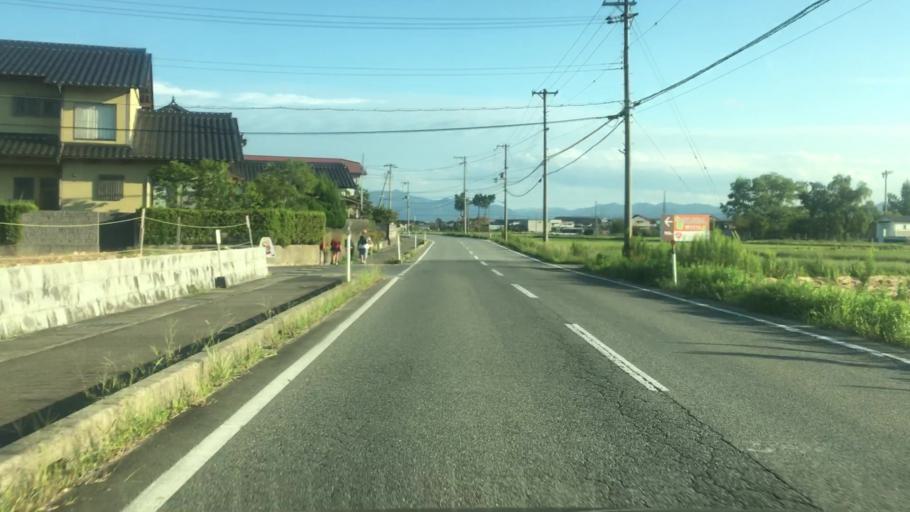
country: JP
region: Hyogo
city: Toyooka
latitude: 35.5642
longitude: 134.8204
